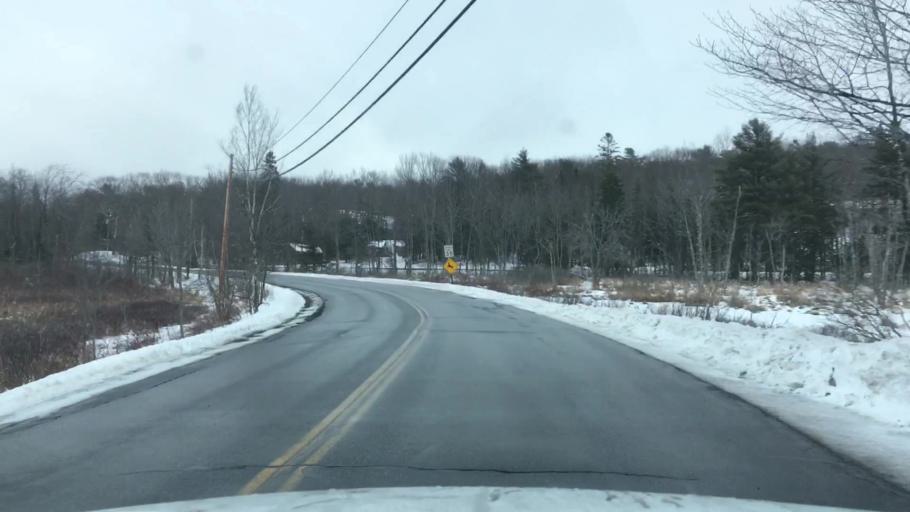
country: US
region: Maine
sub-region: Hancock County
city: Trenton
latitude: 44.4069
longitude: -68.3132
